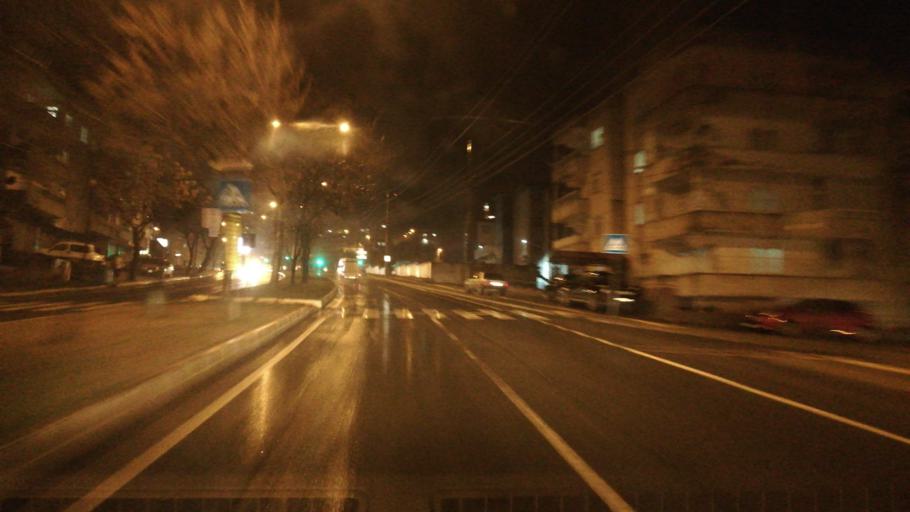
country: TR
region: Kahramanmaras
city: Kahramanmaras
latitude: 37.5852
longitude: 36.9459
